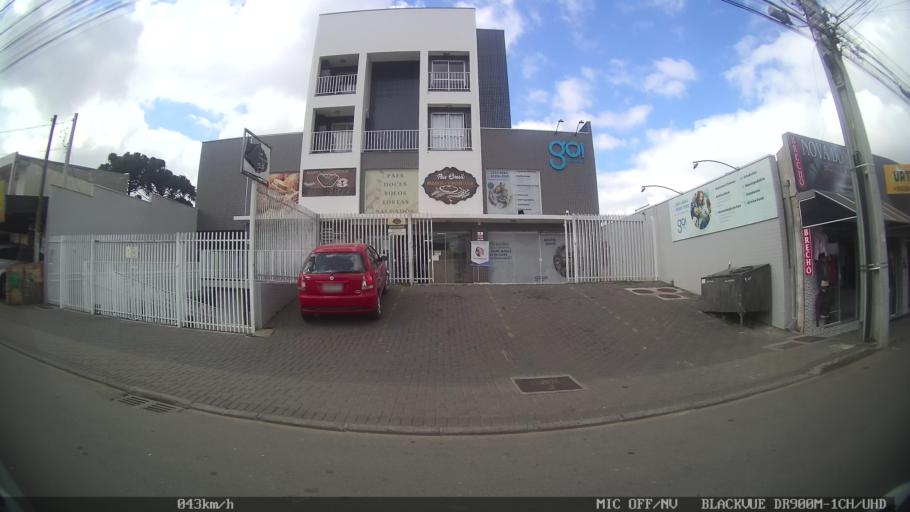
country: BR
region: Parana
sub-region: Pinhais
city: Pinhais
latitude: -25.3697
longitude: -49.2006
